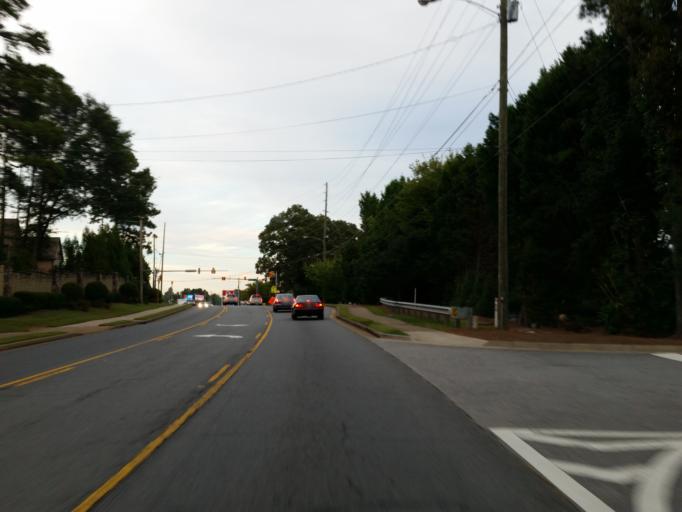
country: US
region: Georgia
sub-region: Fulton County
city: Sandy Springs
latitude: 33.9641
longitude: -84.4174
